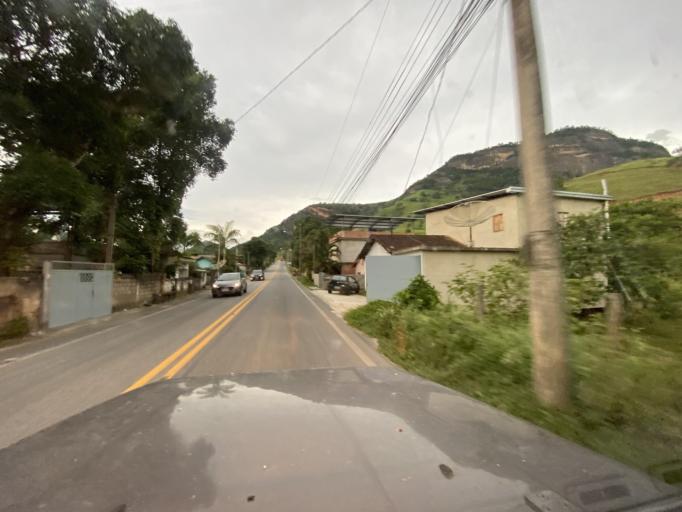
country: BR
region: Espirito Santo
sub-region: Jeronimo Monteiro
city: Jeronimo Monteiro
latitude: -20.8034
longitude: -41.3583
